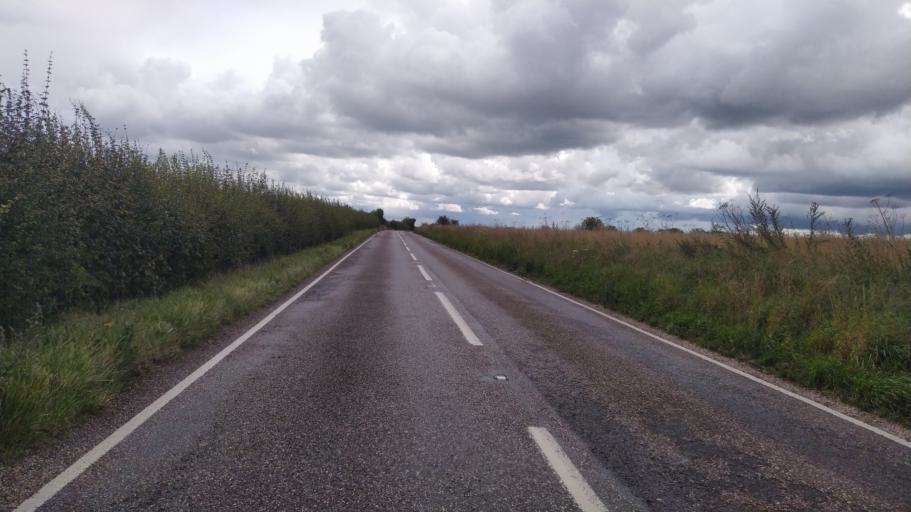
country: GB
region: England
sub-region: Wiltshire
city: Bower Chalke
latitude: 50.9471
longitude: -1.9809
